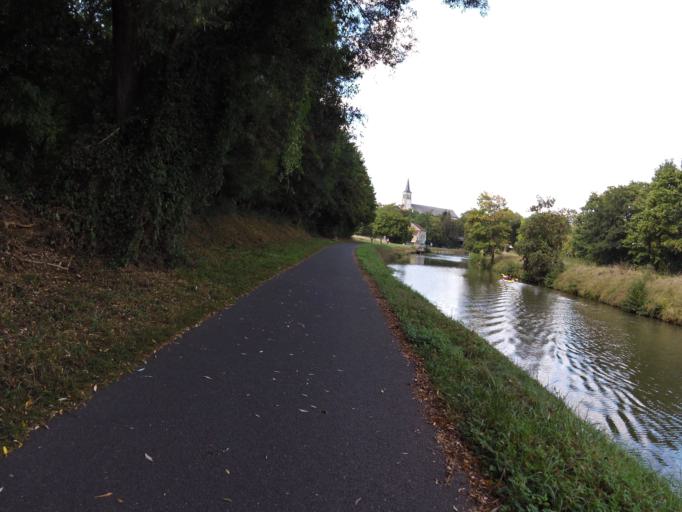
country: DE
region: Saarland
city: Kleinblittersdorf
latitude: 49.1542
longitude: 7.0329
